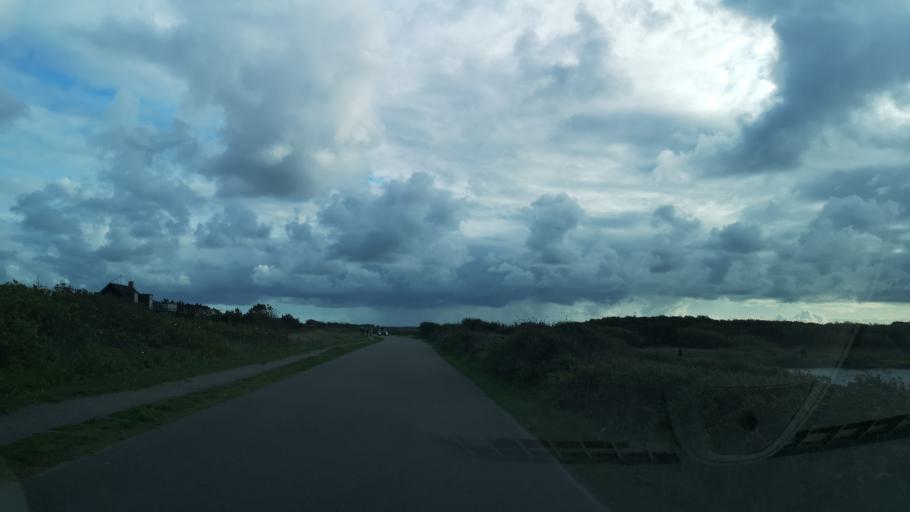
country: DK
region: Central Jutland
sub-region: Ringkobing-Skjern Kommune
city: Ringkobing
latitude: 56.1426
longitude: 8.1329
